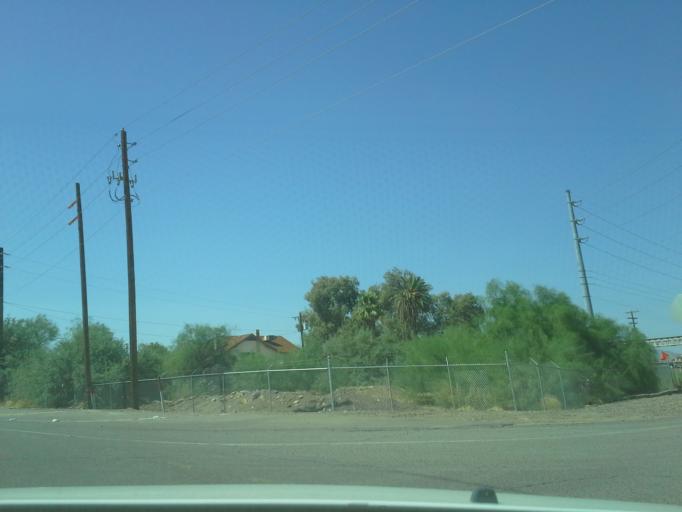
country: US
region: Arizona
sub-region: Maricopa County
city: Laveen
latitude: 33.4035
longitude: -112.1509
